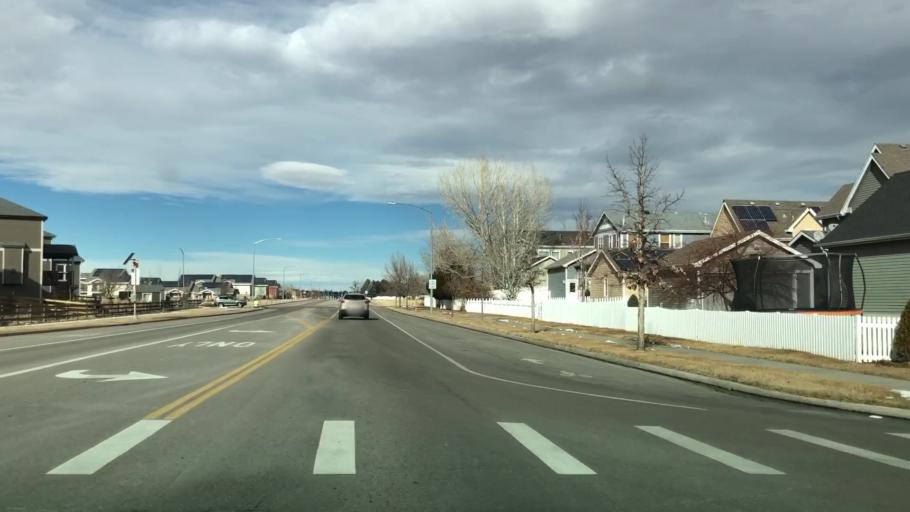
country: US
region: Colorado
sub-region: Weld County
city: Windsor
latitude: 40.4856
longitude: -104.9264
